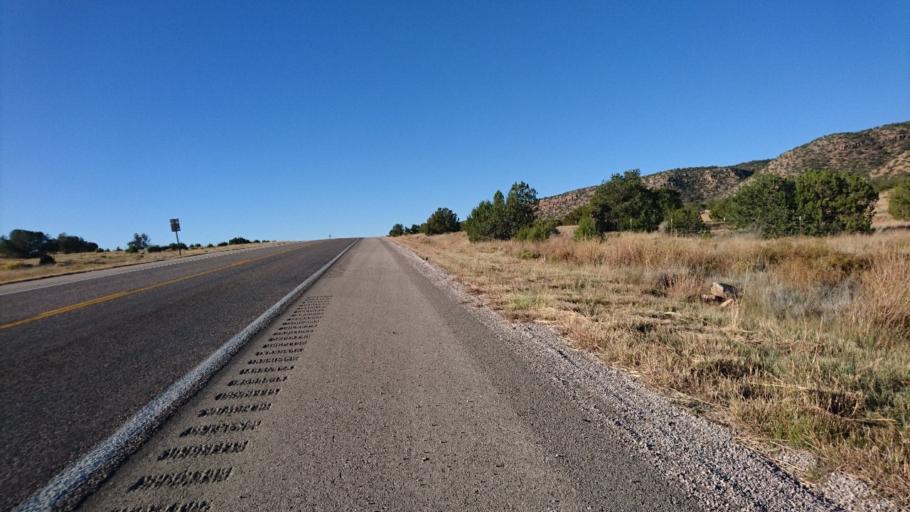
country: US
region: New Mexico
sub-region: Cibola County
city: Grants
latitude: 35.0022
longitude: -107.8944
